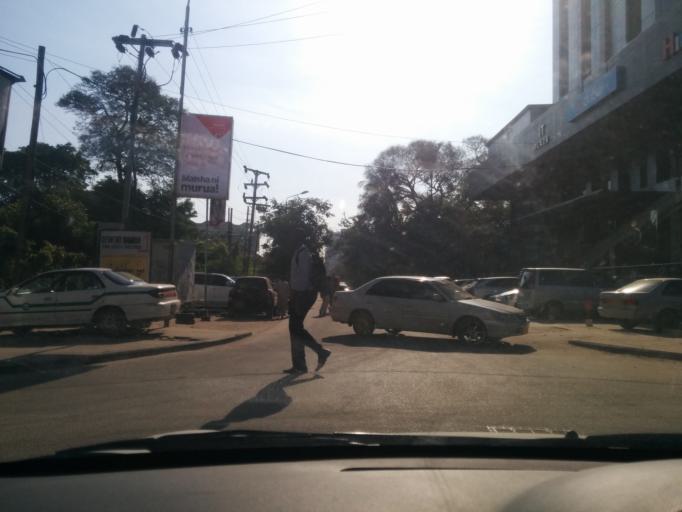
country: TZ
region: Dar es Salaam
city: Dar es Salaam
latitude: -6.8141
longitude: 39.2902
